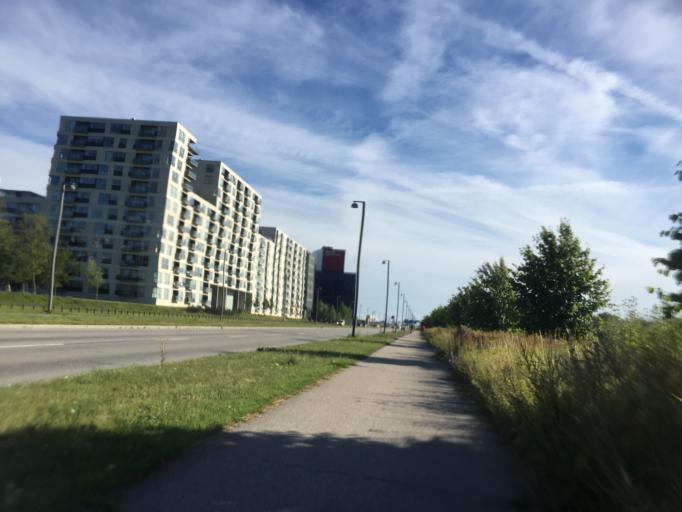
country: DK
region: Capital Region
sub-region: Tarnby Kommune
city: Tarnby
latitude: 55.6343
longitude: 12.5733
